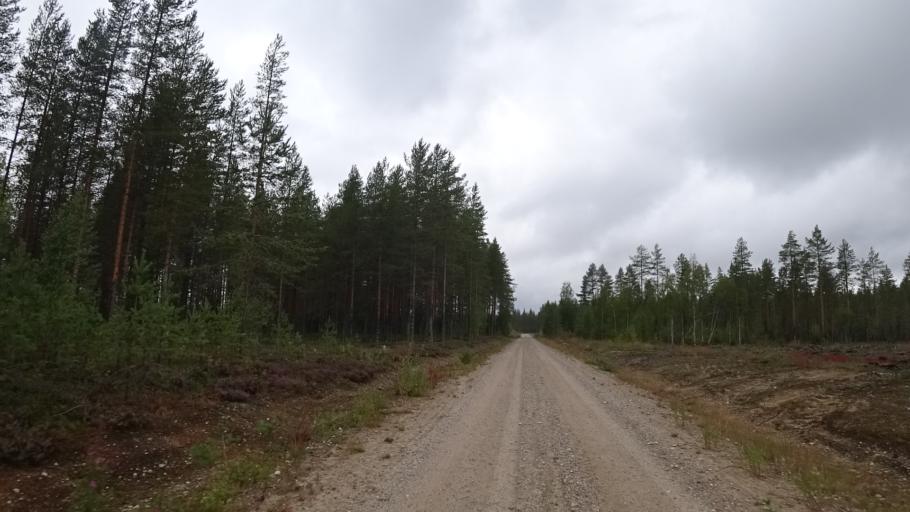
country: FI
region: North Karelia
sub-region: Pielisen Karjala
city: Lieksa
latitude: 63.5196
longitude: 30.1068
